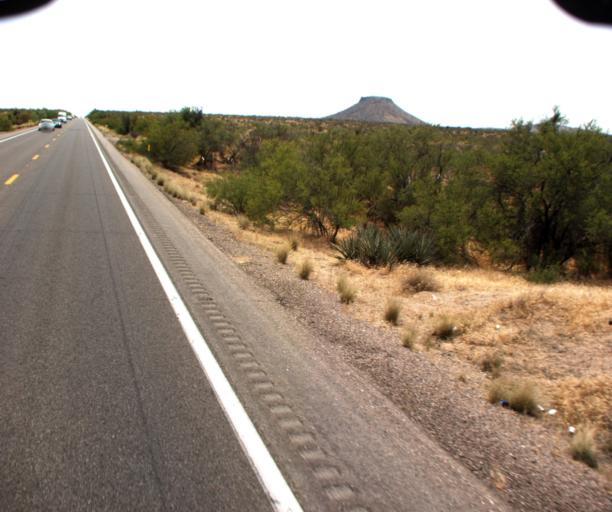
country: US
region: Arizona
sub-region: Gila County
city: San Carlos
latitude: 33.3369
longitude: -110.5890
